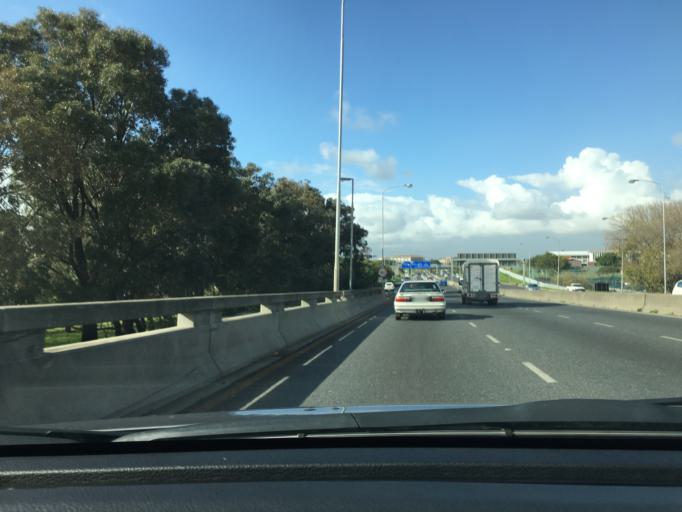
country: ZA
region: Western Cape
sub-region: City of Cape Town
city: Rosebank
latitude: -33.9440
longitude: 18.4775
